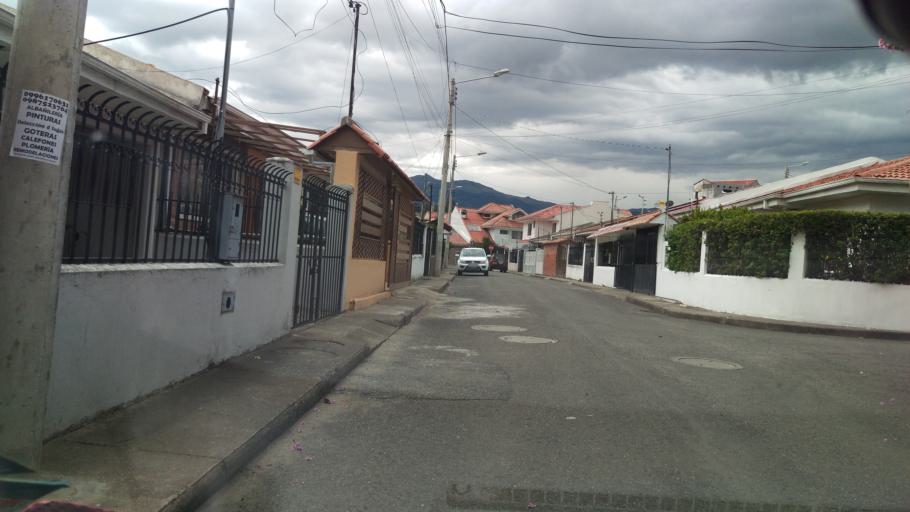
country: EC
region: Azuay
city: Cuenca
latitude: -2.9144
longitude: -79.0057
